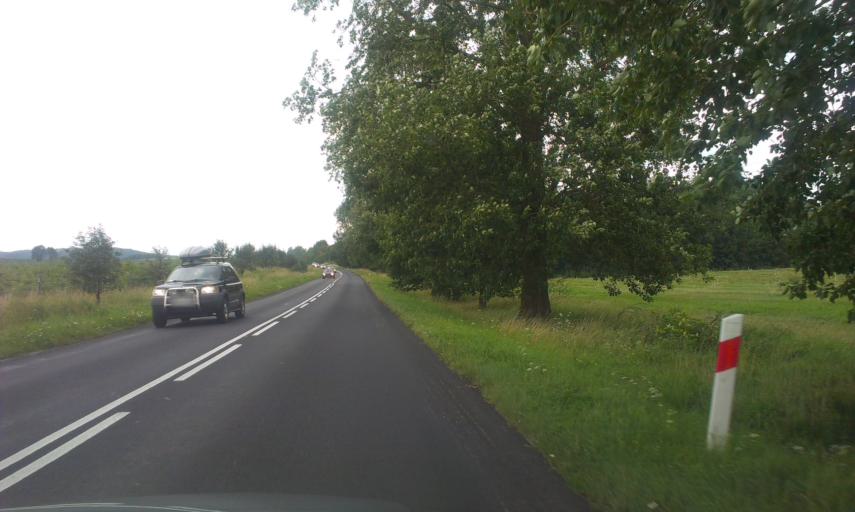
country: PL
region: West Pomeranian Voivodeship
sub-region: Powiat swidwinski
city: Polczyn-Zdroj
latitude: 53.8684
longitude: 16.0703
